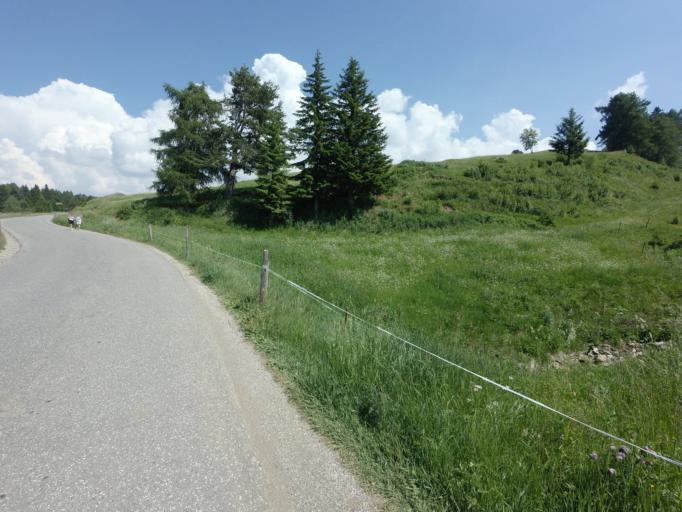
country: IT
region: Trentino-Alto Adige
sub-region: Bolzano
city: Ortisei
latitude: 46.5399
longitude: 11.6266
